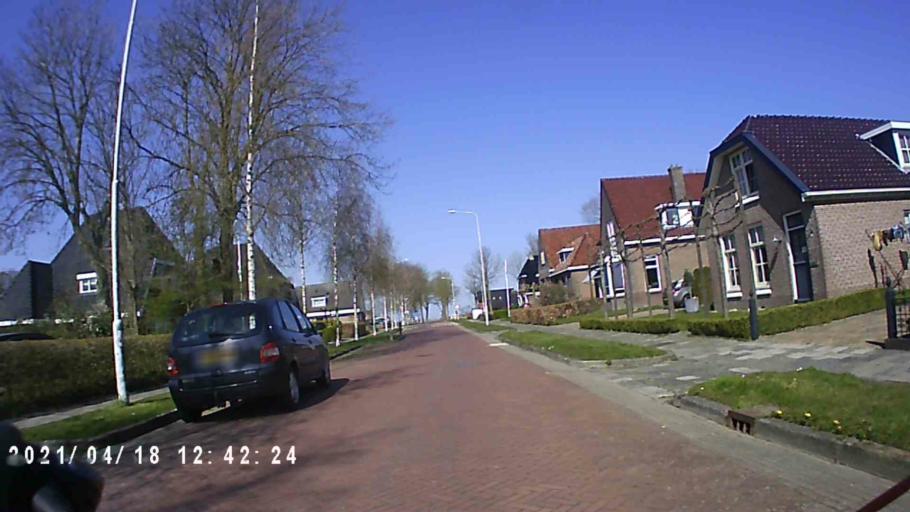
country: NL
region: Friesland
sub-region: Gemeente Dongeradeel
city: Anjum
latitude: 53.3617
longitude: 6.0646
